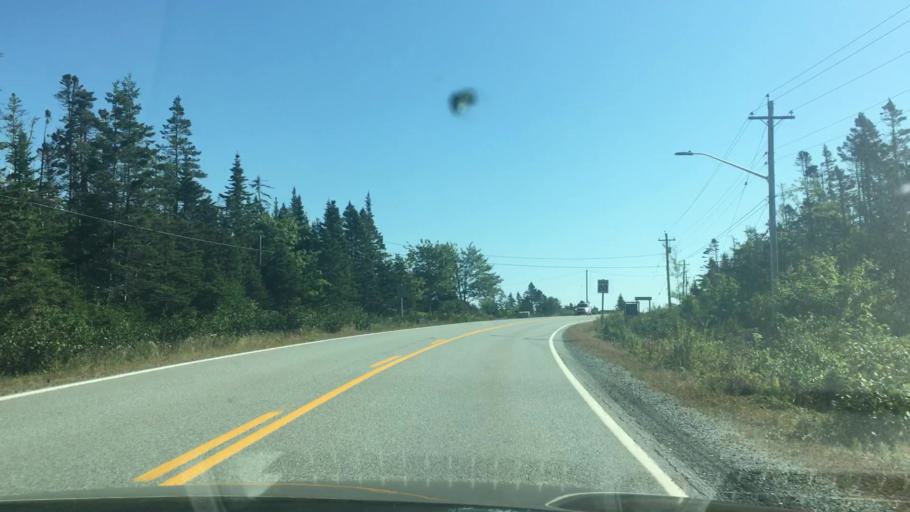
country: CA
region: Nova Scotia
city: Cole Harbour
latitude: 44.7787
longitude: -62.7816
